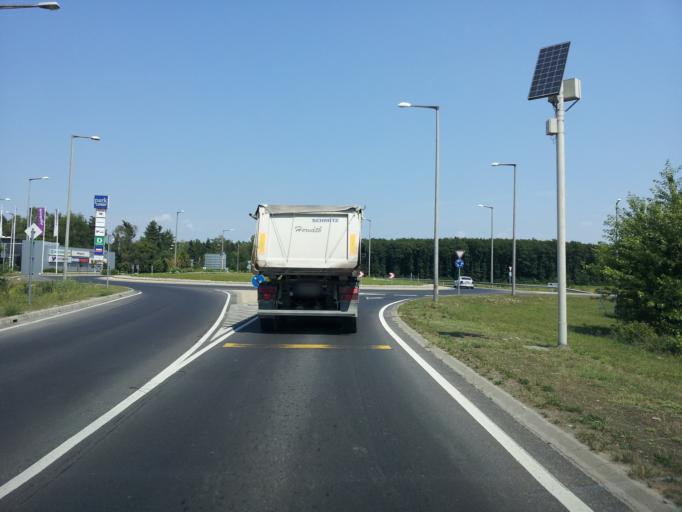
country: HU
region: Zala
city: Zalaegerszeg
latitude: 46.8450
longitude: 16.8656
